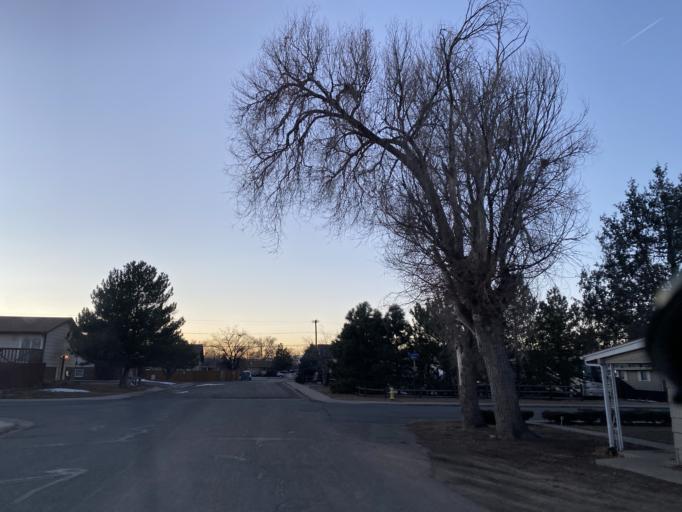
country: US
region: Colorado
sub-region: Adams County
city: Brighton
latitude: 39.9759
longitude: -104.8164
